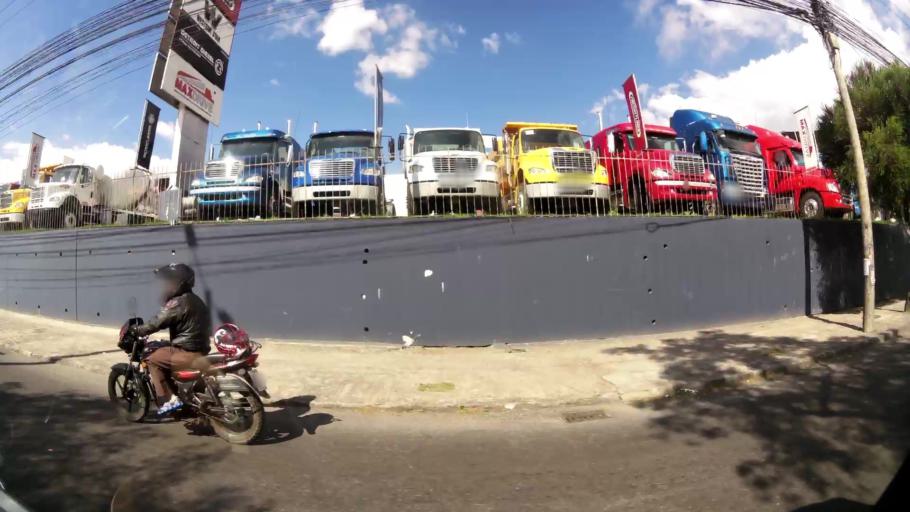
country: EC
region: Pichincha
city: Quito
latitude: -0.1128
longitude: -78.4789
